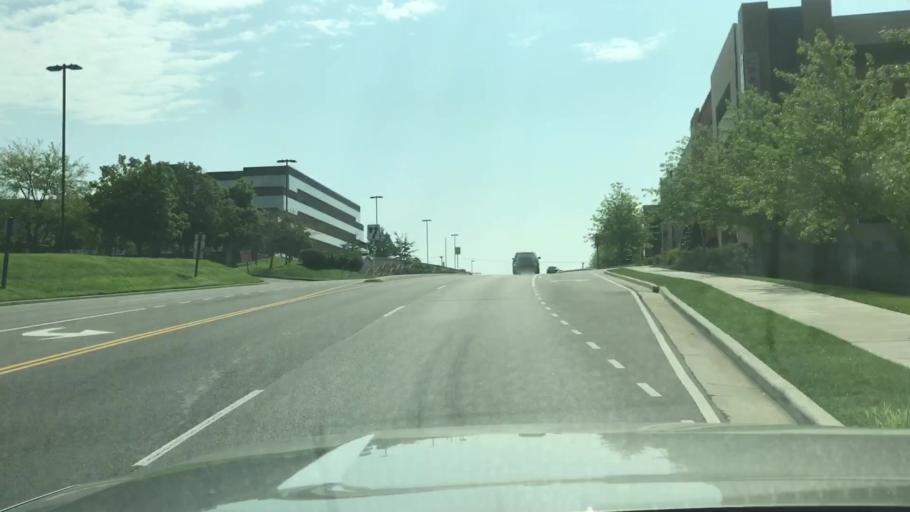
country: US
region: Tennessee
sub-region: Williamson County
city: Brentwood
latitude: 36.0342
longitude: -86.7915
